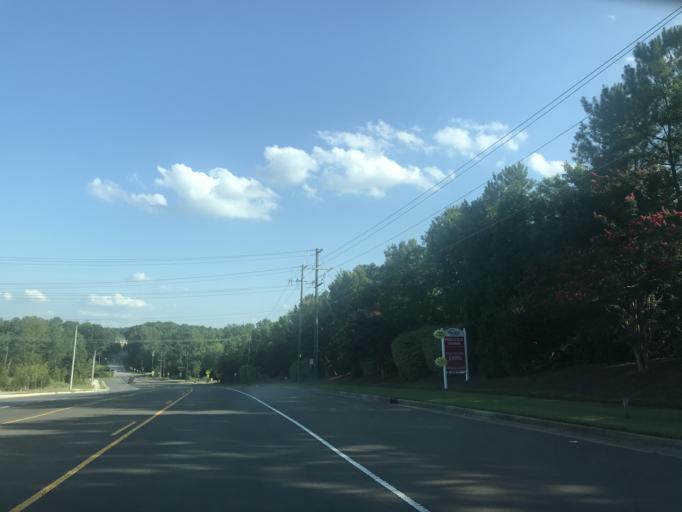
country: US
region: North Carolina
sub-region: Wake County
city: Knightdale
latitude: 35.7800
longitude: -78.5272
